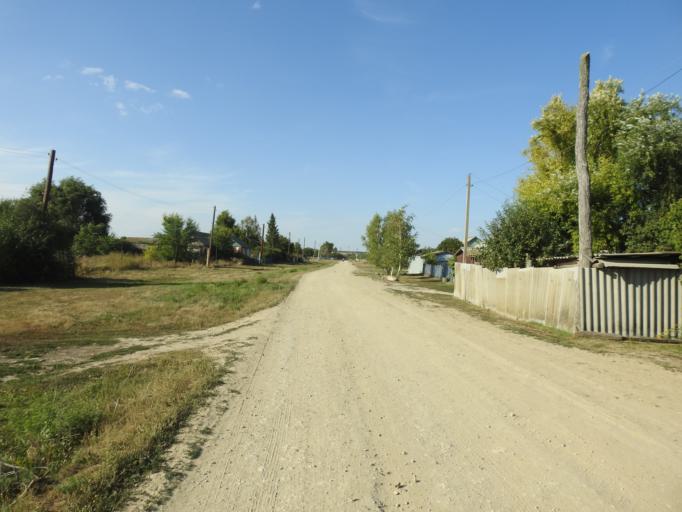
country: RU
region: Volgograd
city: Zhirnovsk
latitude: 51.2168
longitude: 44.9437
